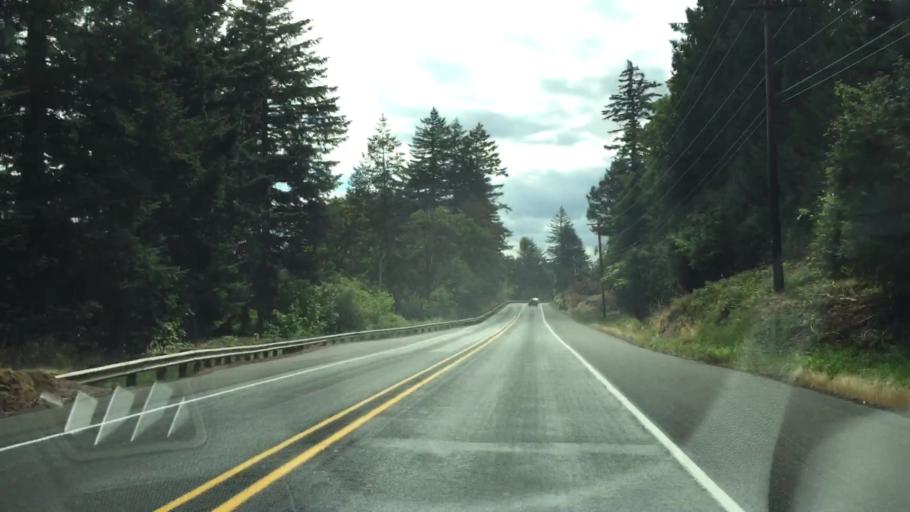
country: US
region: Washington
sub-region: Clark County
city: Washougal
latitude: 45.5931
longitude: -122.1374
